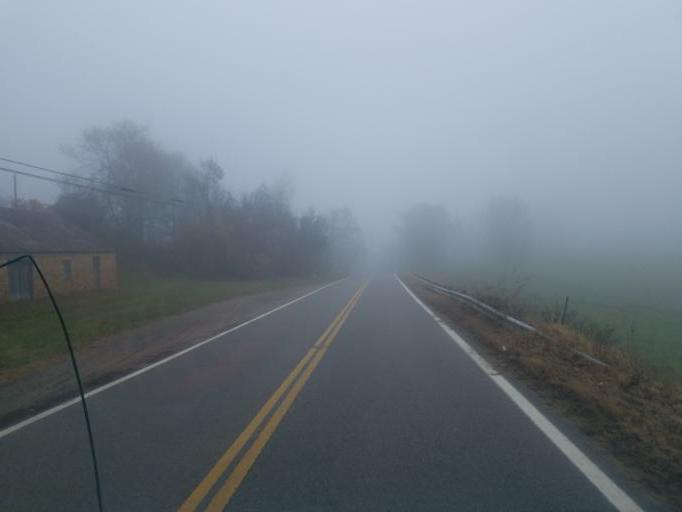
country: US
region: Ohio
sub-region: Morgan County
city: McConnelsville
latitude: 39.6290
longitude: -81.8782
